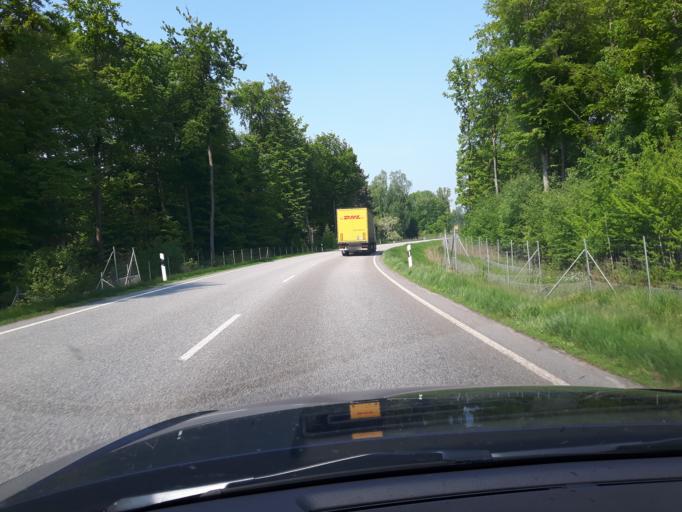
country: DE
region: Schleswig-Holstein
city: Ratekau
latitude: 53.8848
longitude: 10.7674
